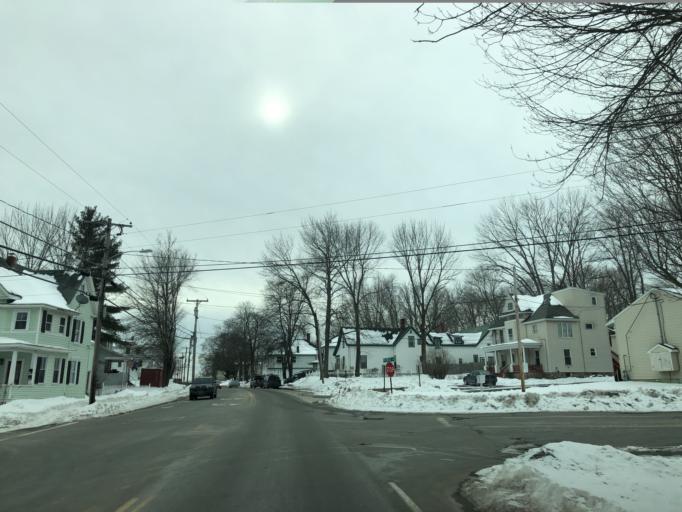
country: US
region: Maine
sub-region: Cumberland County
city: Westbrook
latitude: 43.6838
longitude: -70.3658
